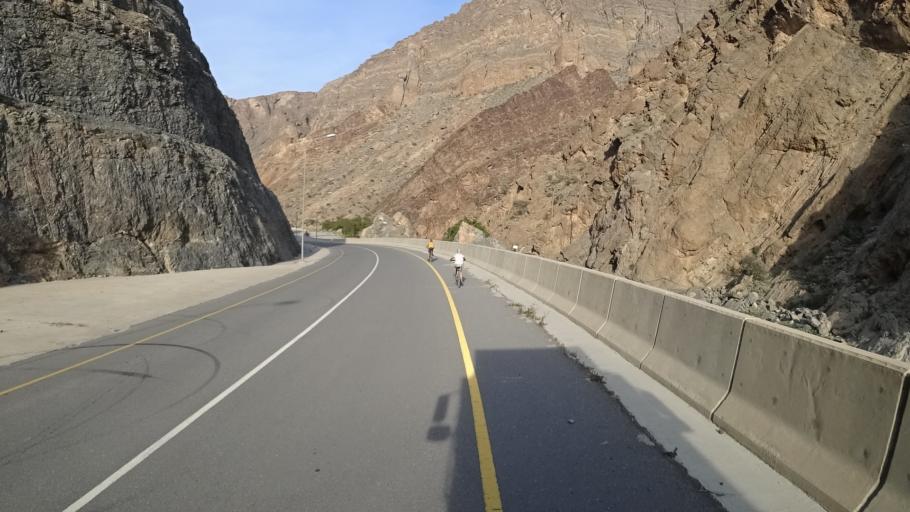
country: OM
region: Al Batinah
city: Bayt al `Awabi
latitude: 23.2789
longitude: 57.4625
